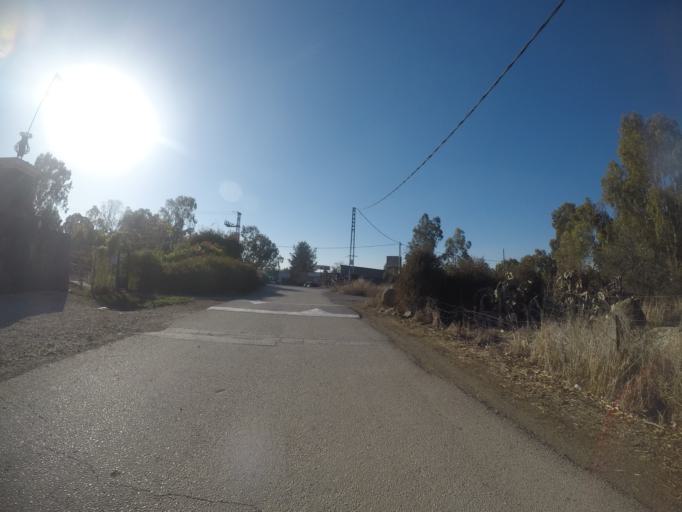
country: SY
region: Quneitra
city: Fiq
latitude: 32.8074
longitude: 35.7410
